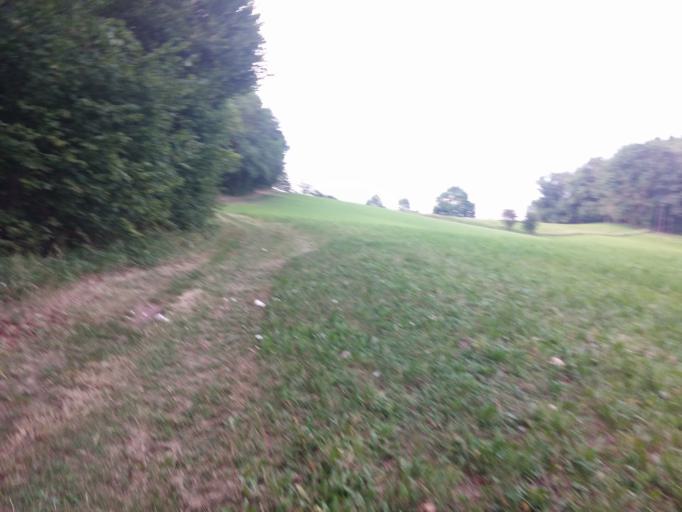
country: DE
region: Bavaria
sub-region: Swabia
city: Woringen
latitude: 47.8680
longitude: 10.1947
